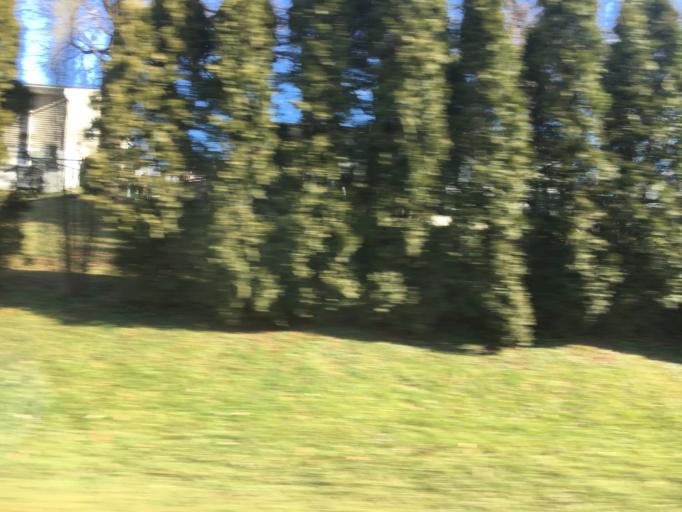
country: US
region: Pennsylvania
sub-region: Lehigh County
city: Stiles
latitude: 40.6349
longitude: -75.5083
